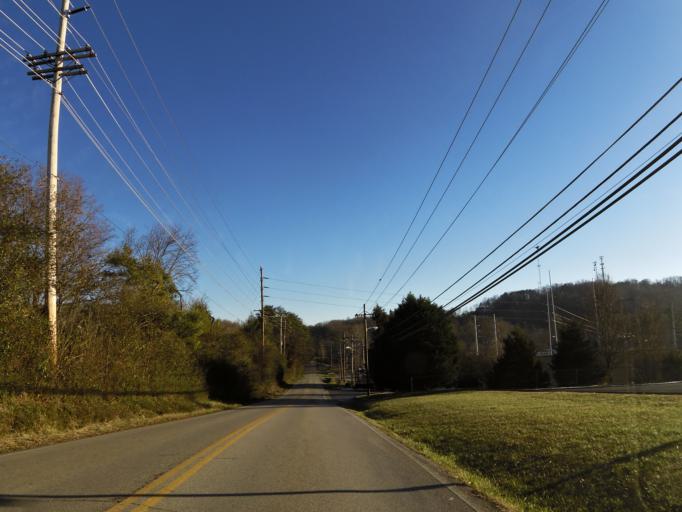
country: US
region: Tennessee
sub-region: Knox County
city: Farragut
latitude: 35.8930
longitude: -84.1359
